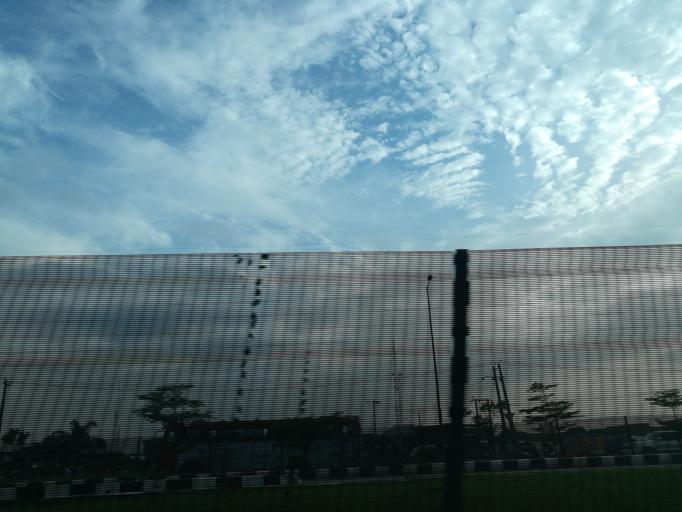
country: NG
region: Lagos
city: Ojota
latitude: 6.6105
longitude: 3.4211
